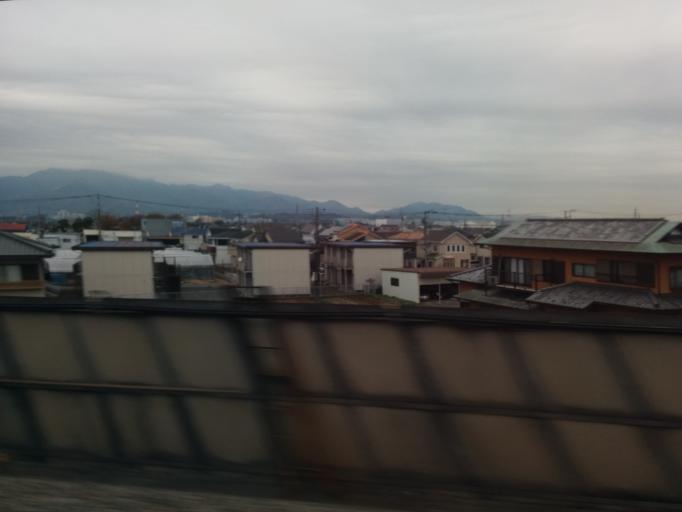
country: JP
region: Kanagawa
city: Atsugi
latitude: 35.3880
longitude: 139.3661
